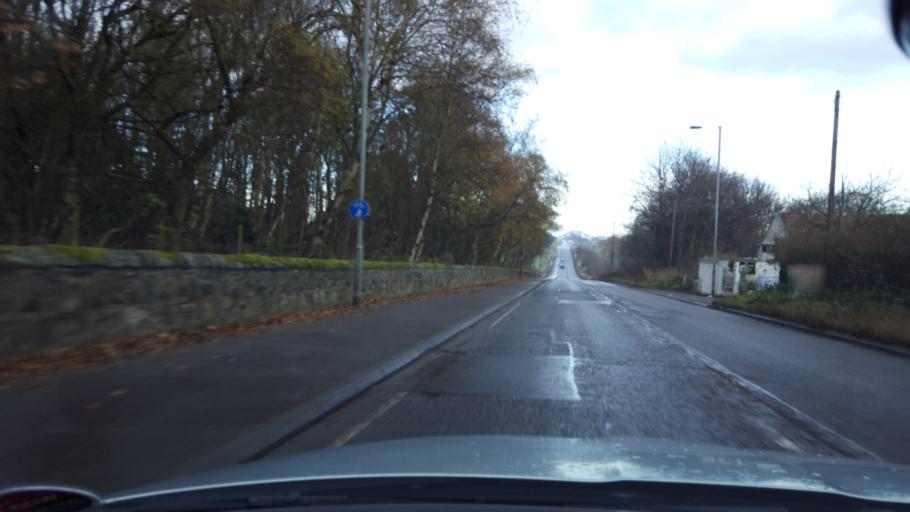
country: GB
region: Scotland
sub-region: Edinburgh
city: Kirkliston
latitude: 55.9719
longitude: -3.4001
